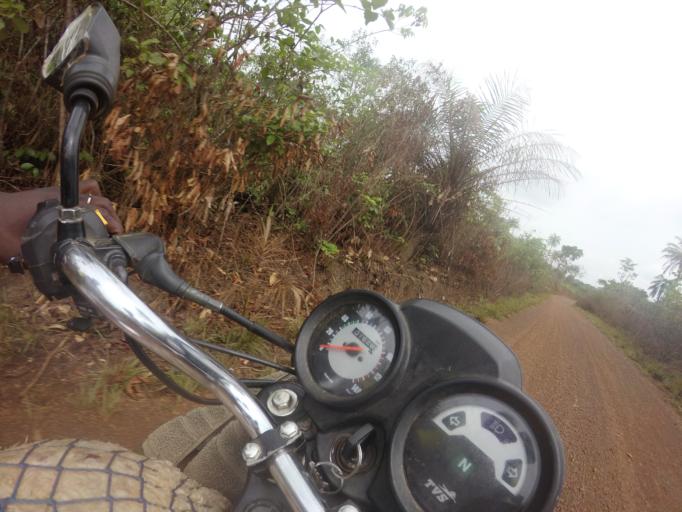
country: SL
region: Southern Province
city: Zimmi
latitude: 7.1754
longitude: -11.2345
